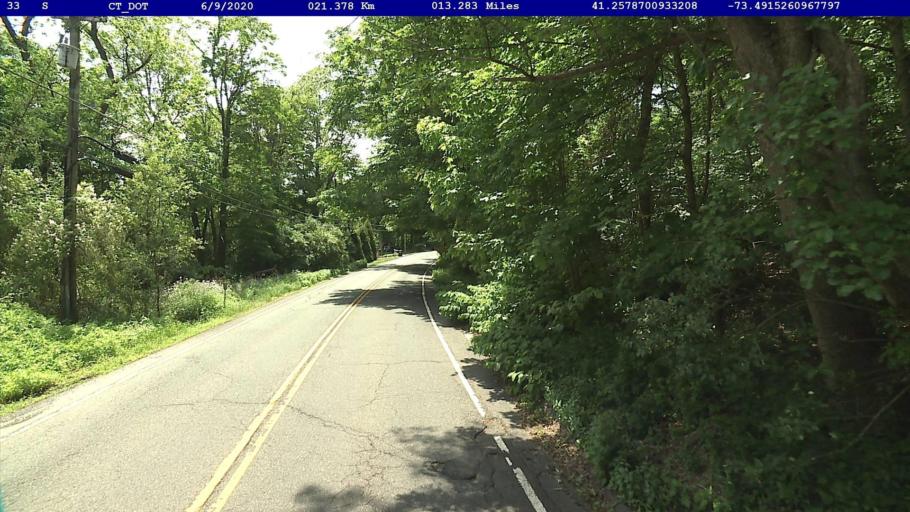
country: US
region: Connecticut
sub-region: Fairfield County
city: Ridgefield
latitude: 41.2578
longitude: -73.4916
